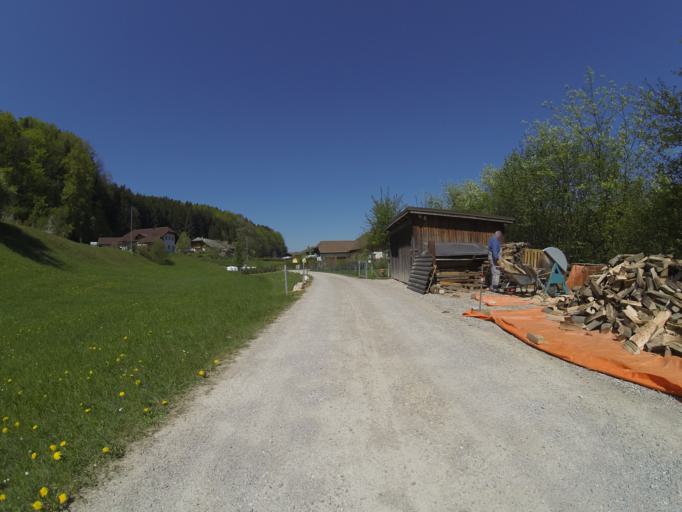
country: AT
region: Upper Austria
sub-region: Politischer Bezirk Gmunden
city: Altmunster
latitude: 47.9333
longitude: 13.7533
